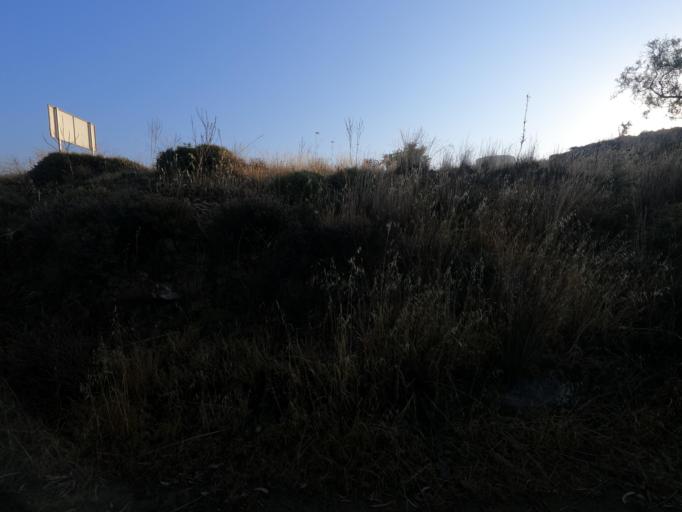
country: CY
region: Larnaka
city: Mosfiloti
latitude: 34.9747
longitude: 33.4208
